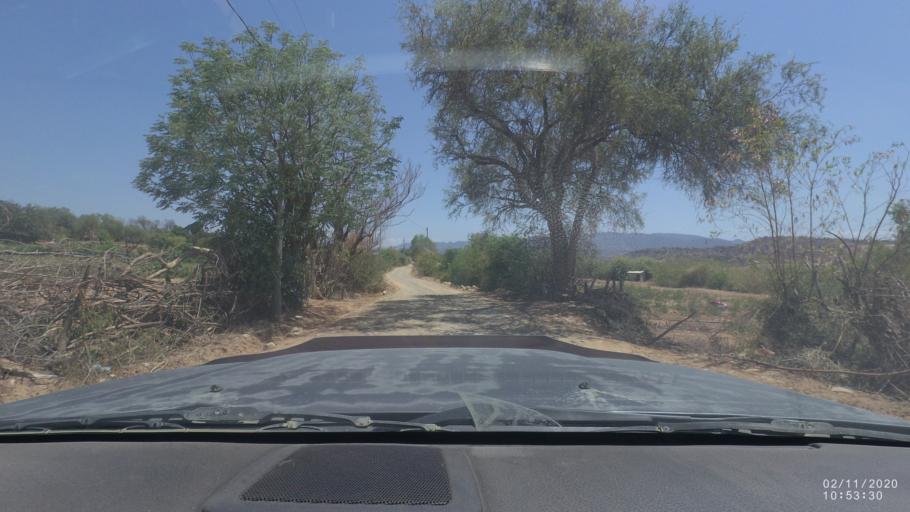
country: BO
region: Cochabamba
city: Aiquile
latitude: -18.1783
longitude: -64.8693
